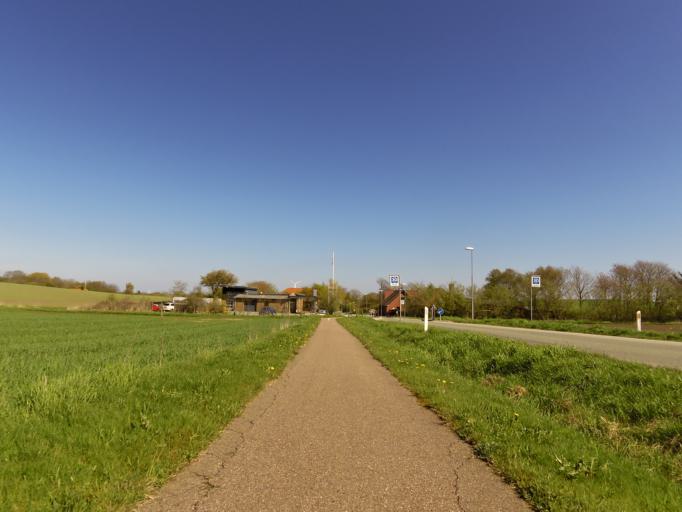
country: DK
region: Central Jutland
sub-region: Holstebro Kommune
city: Vinderup
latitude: 56.6002
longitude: 8.7543
